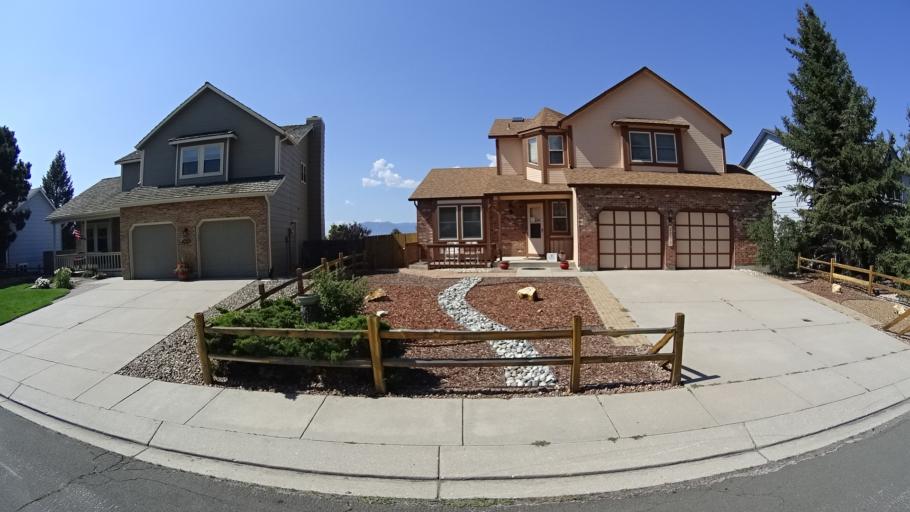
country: US
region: Colorado
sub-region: El Paso County
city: Black Forest
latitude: 38.9553
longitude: -104.7746
